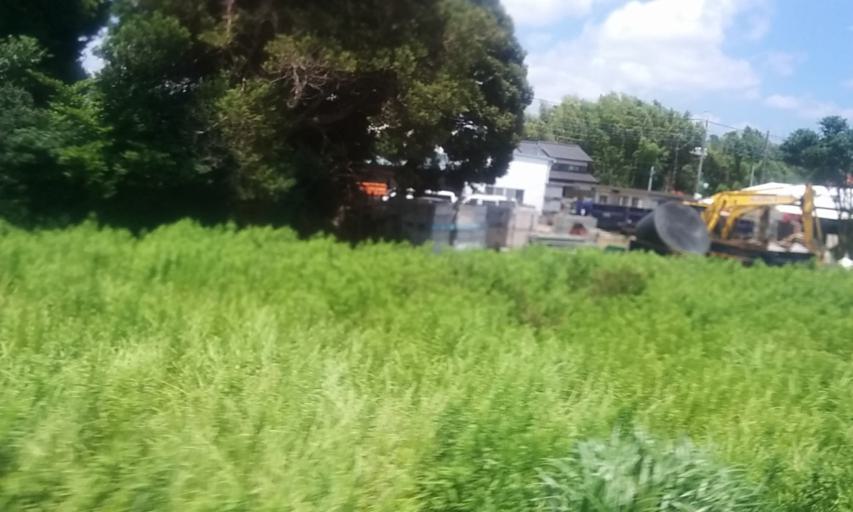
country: JP
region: Chiba
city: Oami
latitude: 35.5406
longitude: 140.2361
